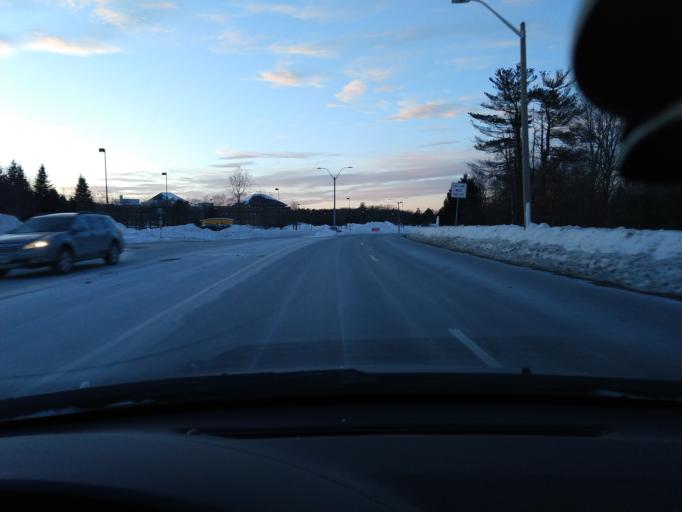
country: US
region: Massachusetts
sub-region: Middlesex County
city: Pinehurst
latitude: 42.4973
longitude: -71.2304
